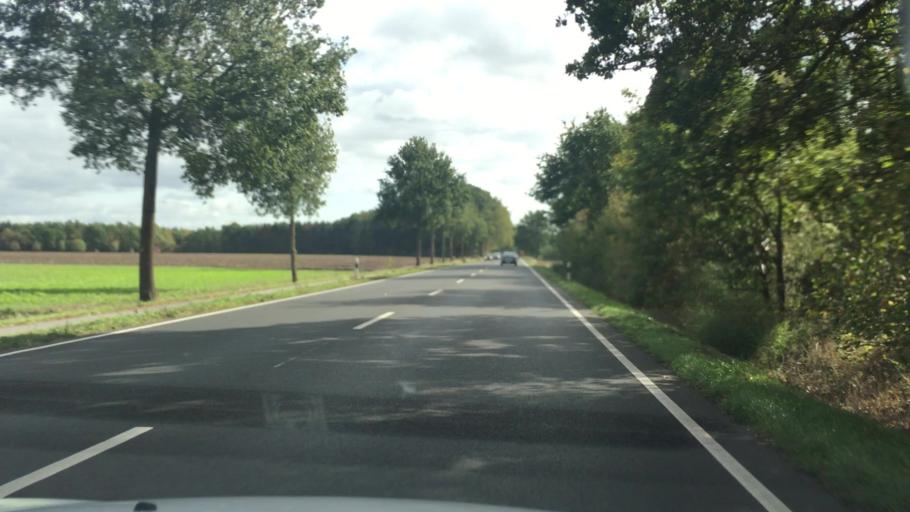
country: DE
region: Lower Saxony
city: Diepholz
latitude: 52.6334
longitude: 8.3563
